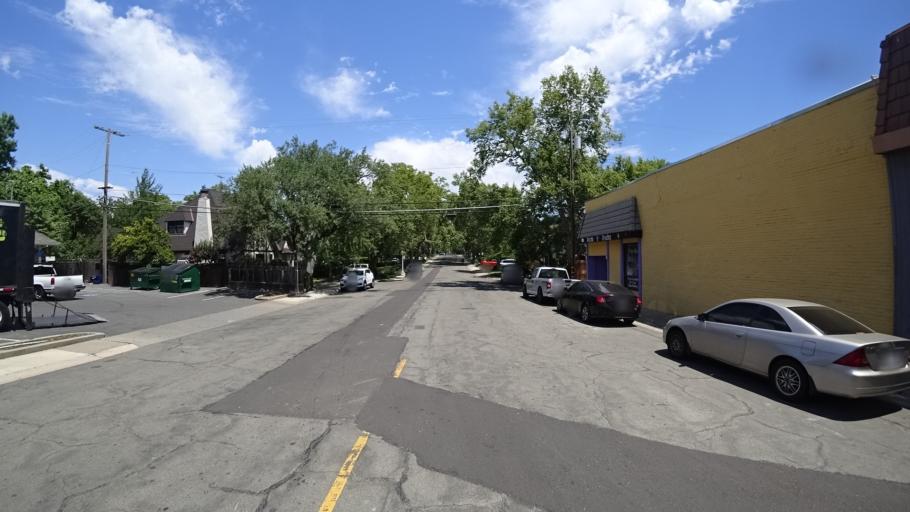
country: US
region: California
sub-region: Sacramento County
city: Sacramento
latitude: 38.5703
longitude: -121.4447
